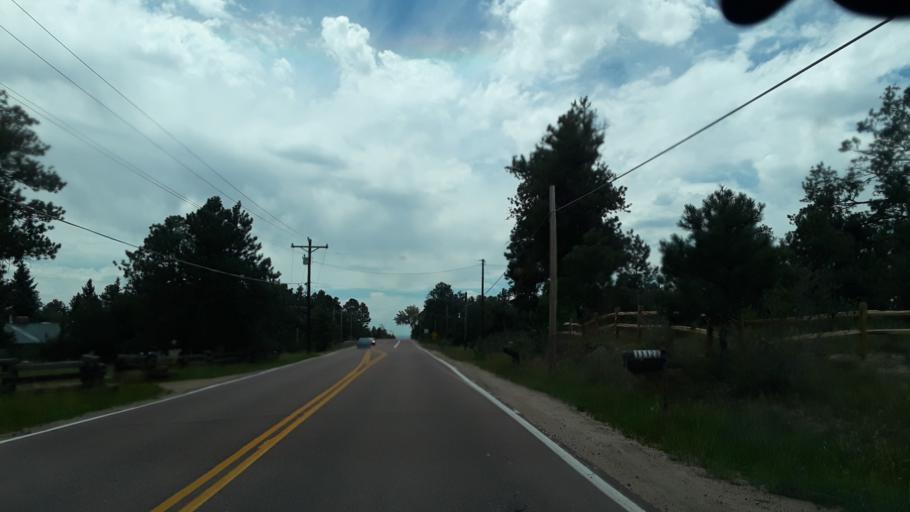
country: US
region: Colorado
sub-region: El Paso County
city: Black Forest
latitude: 38.9925
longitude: -104.7004
